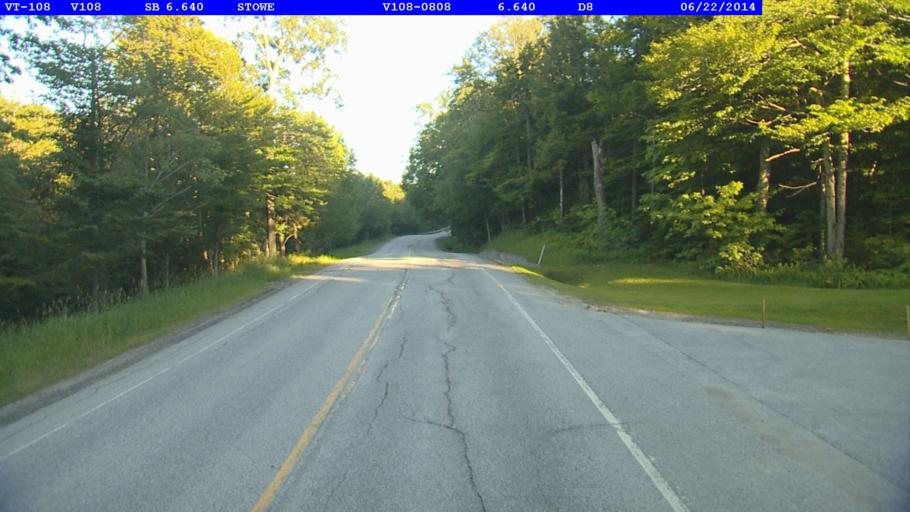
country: US
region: Vermont
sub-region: Lamoille County
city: Johnson
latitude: 44.5202
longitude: -72.7712
